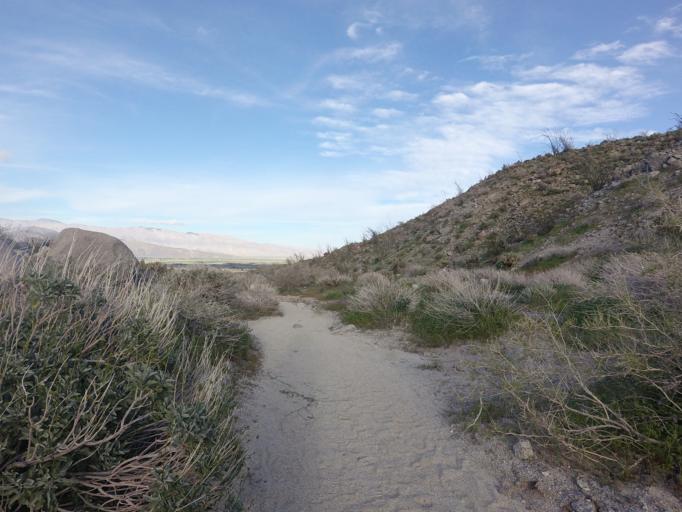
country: US
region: California
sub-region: San Diego County
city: Borrego Springs
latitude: 33.2430
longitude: -116.4228
